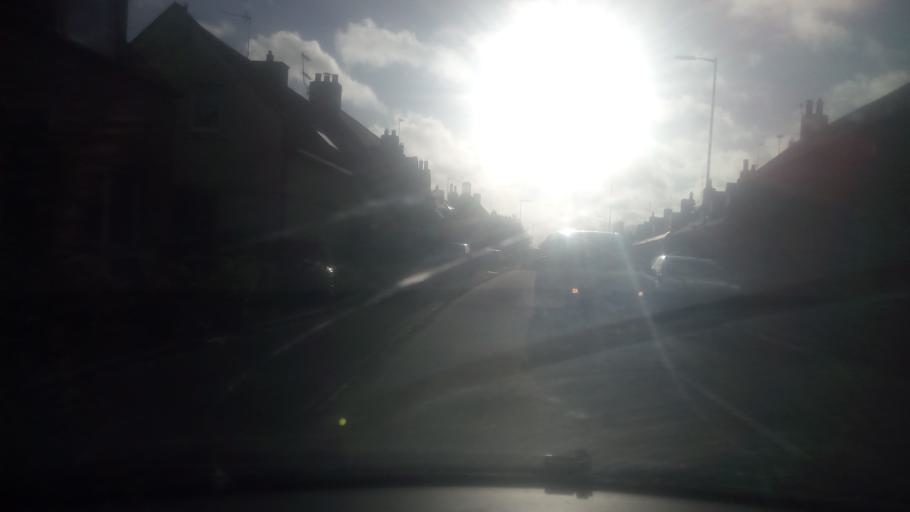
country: GB
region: Scotland
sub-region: The Scottish Borders
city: Duns
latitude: 55.6913
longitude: -2.3329
